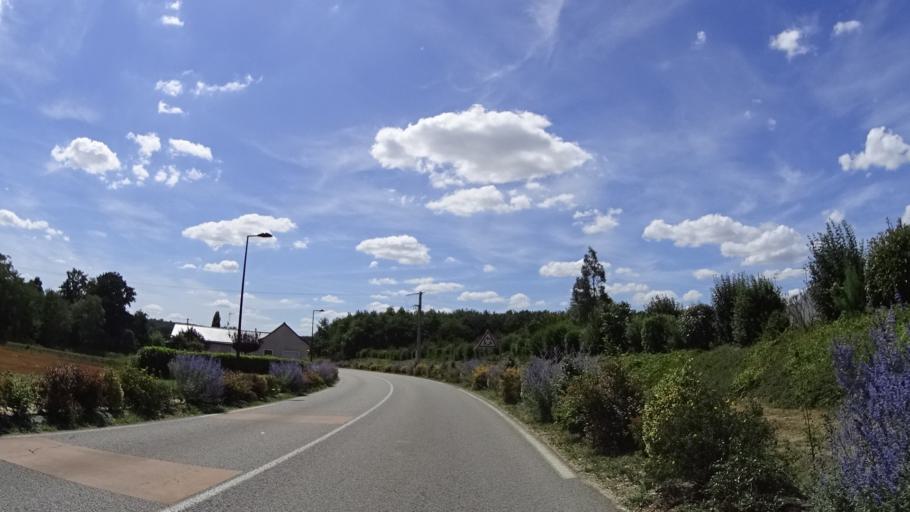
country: FR
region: Pays de la Loire
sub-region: Departement de Maine-et-Loire
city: Cande
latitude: 47.6143
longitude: -0.9834
